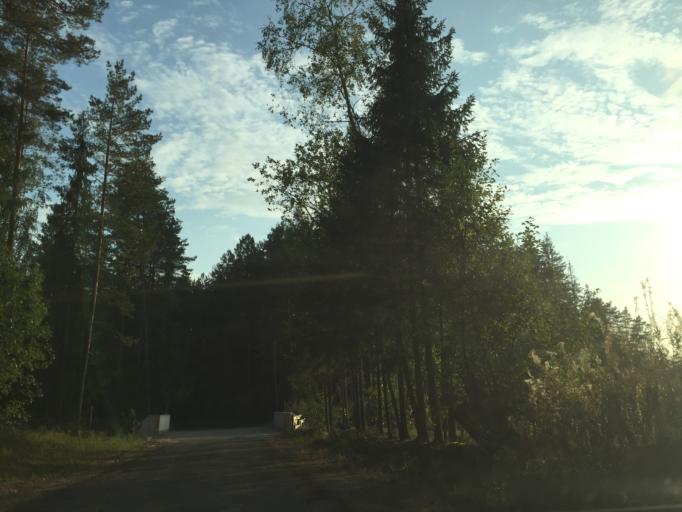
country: LV
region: Baldone
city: Baldone
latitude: 56.7733
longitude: 24.4002
